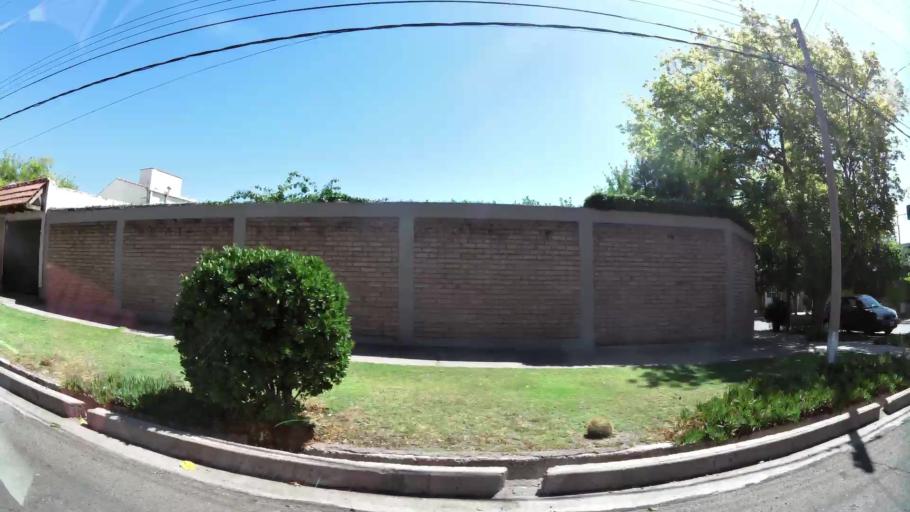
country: AR
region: Mendoza
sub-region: Departamento de Godoy Cruz
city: Godoy Cruz
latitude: -32.9396
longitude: -68.8576
